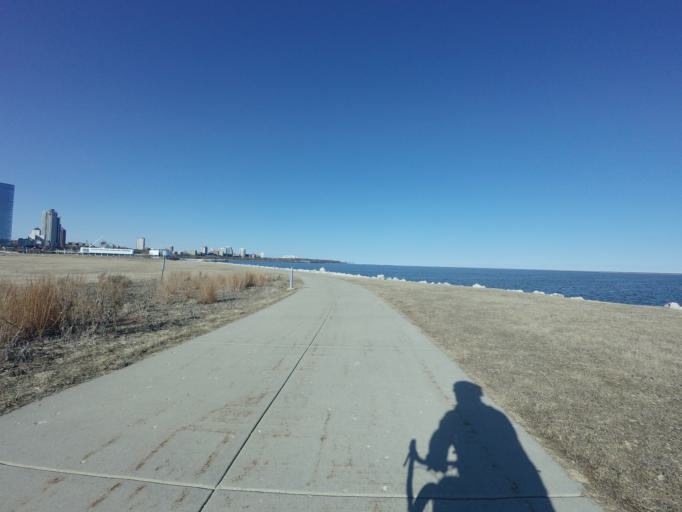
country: US
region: Wisconsin
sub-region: Milwaukee County
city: Milwaukee
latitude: 43.0308
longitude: -87.8945
